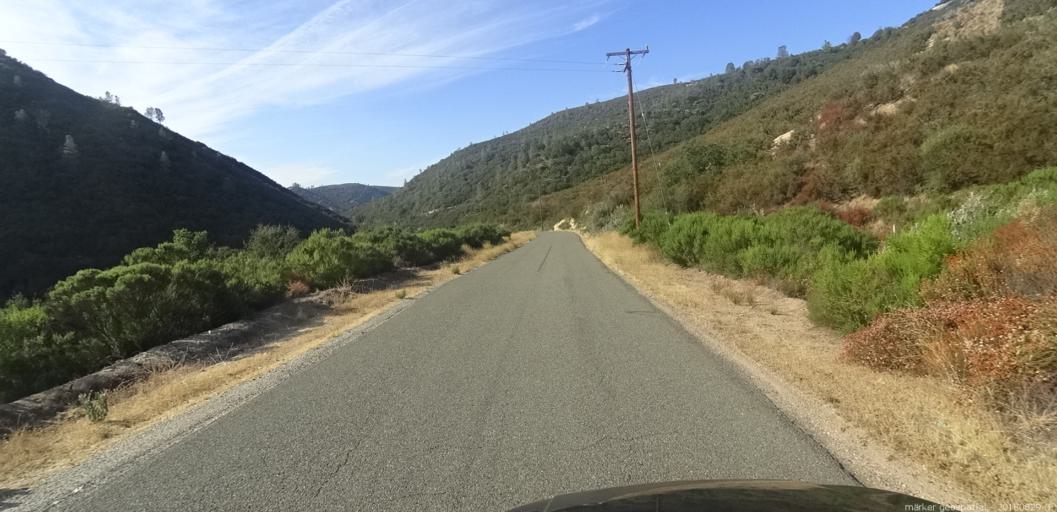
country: US
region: California
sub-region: Monterey County
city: King City
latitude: 36.0161
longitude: -121.0677
